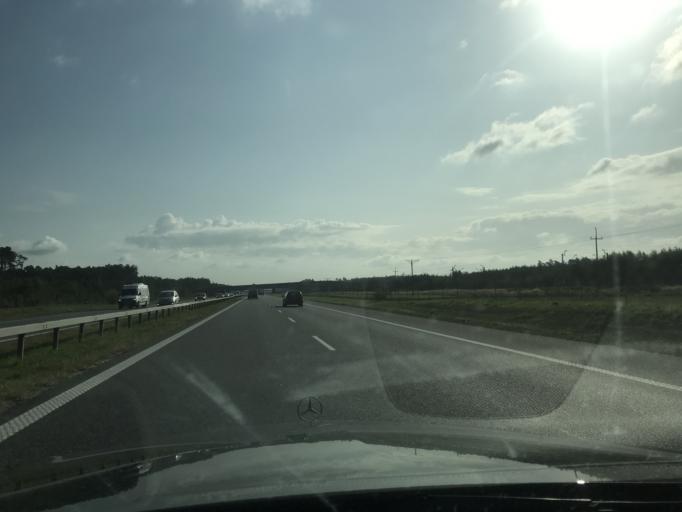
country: PL
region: Lesser Poland Voivodeship
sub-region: Powiat brzeski
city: Debno
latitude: 50.0056
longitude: 20.7803
